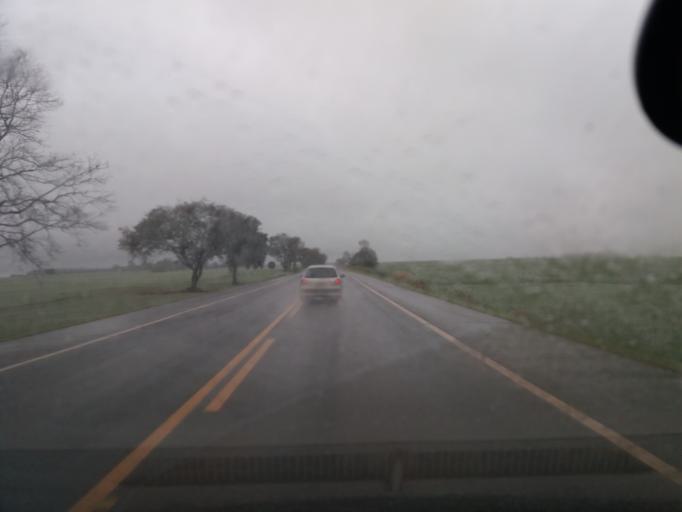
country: BR
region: Parana
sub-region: Campo Mourao
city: Campo Mourao
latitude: -24.3054
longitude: -52.6041
